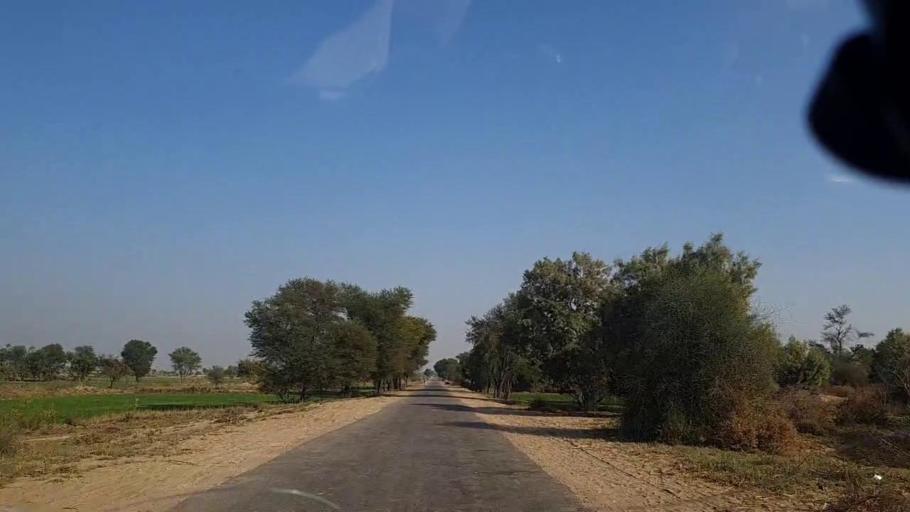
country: PK
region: Sindh
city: Khanpur
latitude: 27.6882
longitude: 69.5002
